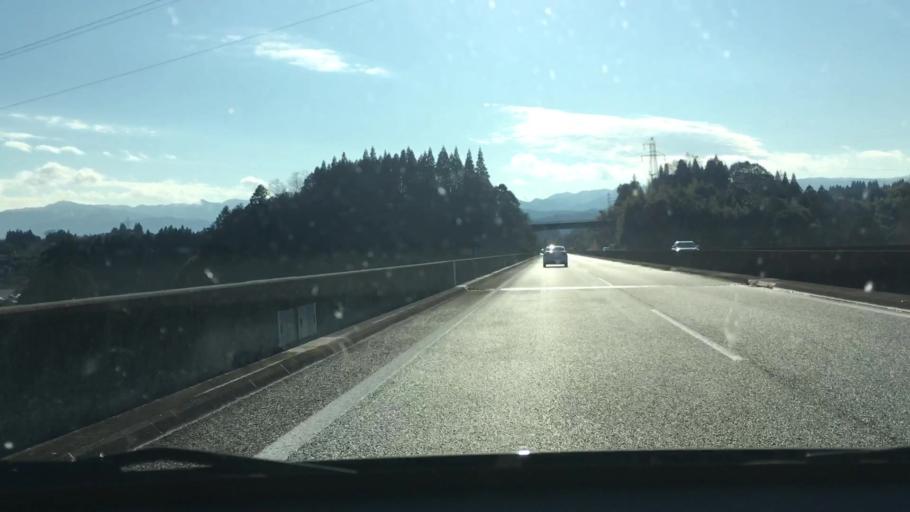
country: JP
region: Kumamoto
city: Hitoyoshi
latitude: 32.2138
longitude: 130.7772
